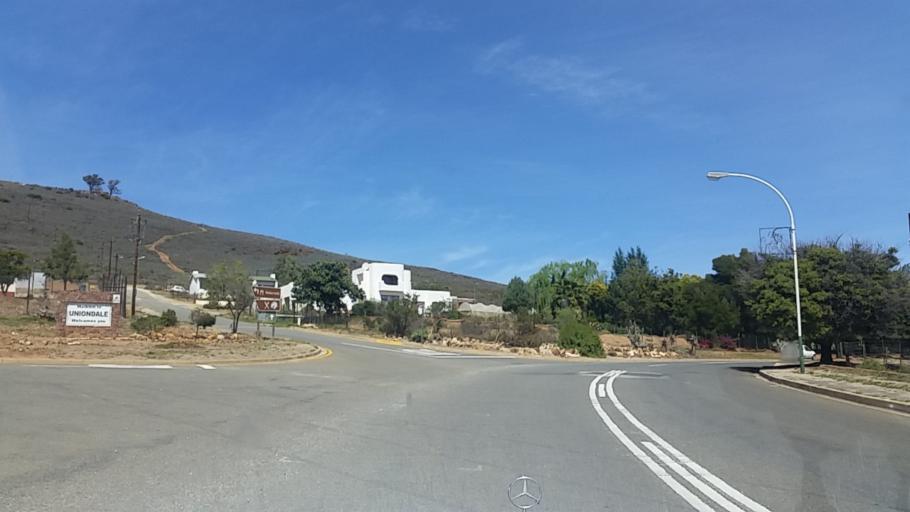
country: ZA
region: Western Cape
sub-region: Eden District Municipality
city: Knysna
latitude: -33.6552
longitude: 23.1346
